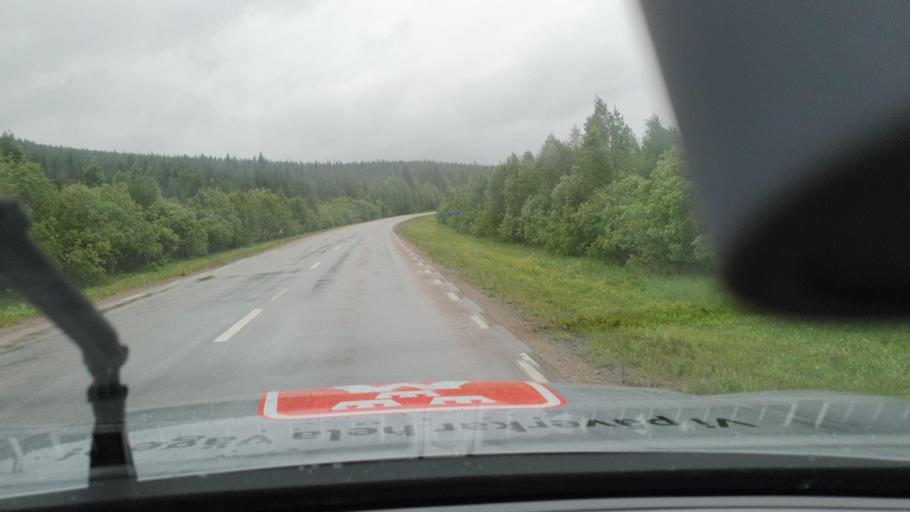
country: SE
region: Norrbotten
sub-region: Overtornea Kommun
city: OEvertornea
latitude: 66.4377
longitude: 23.3276
